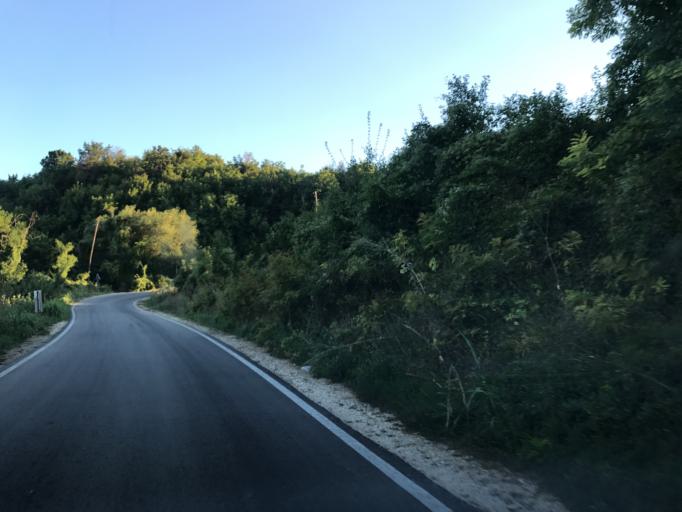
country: BG
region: Vidin
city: Bregovo
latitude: 44.1309
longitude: 22.6034
